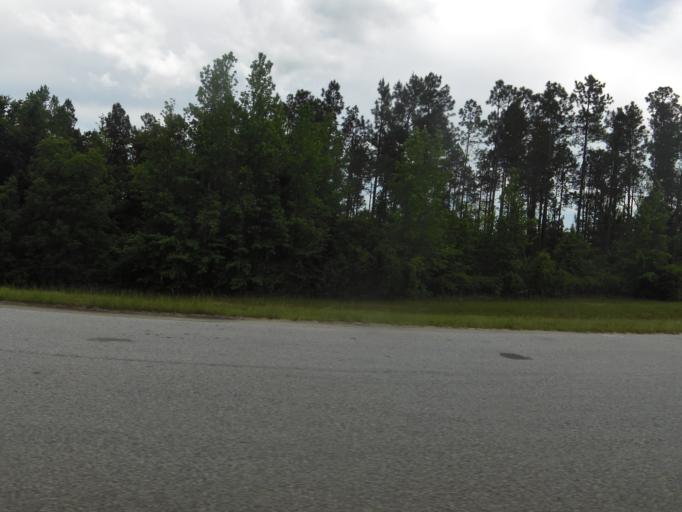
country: US
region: Georgia
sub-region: Emanuel County
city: Swainsboro
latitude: 32.6375
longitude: -82.3699
